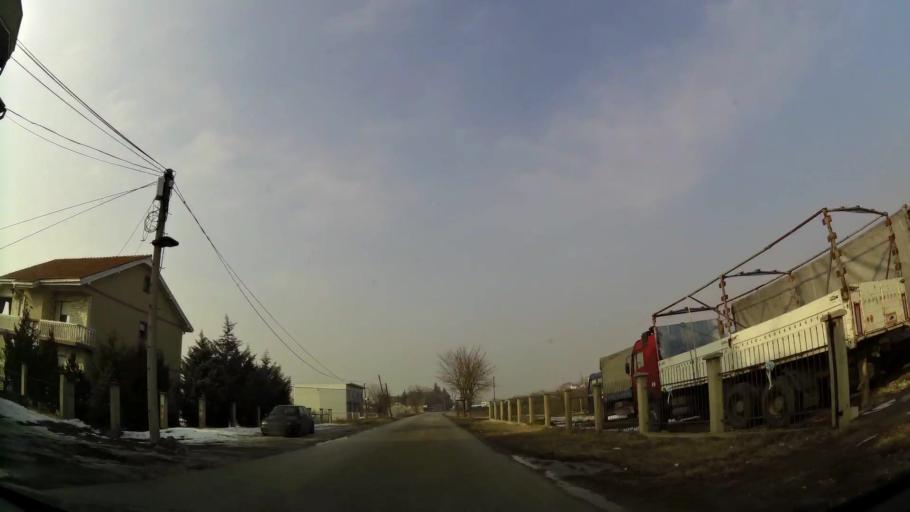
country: MK
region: Ilinden
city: Marino
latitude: 41.9820
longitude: 21.5963
